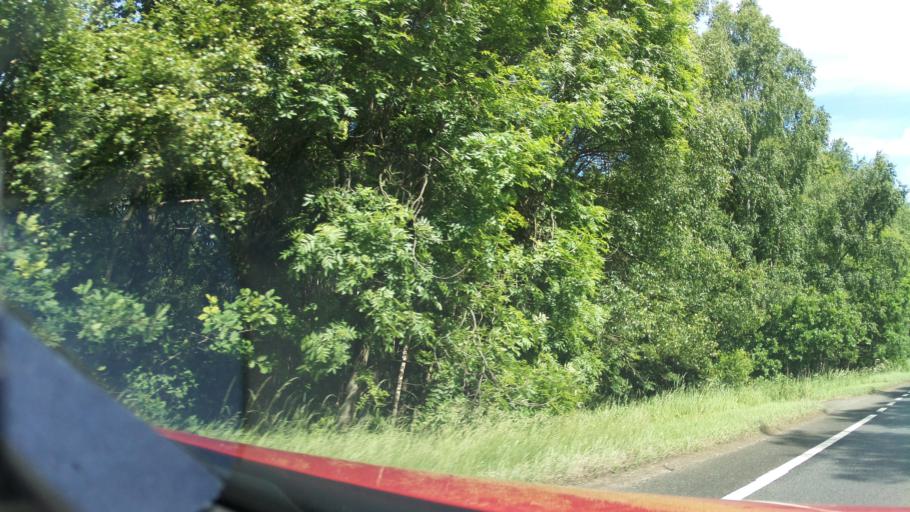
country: GB
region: England
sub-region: Lincolnshire
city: Skellingthorpe
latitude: 53.2171
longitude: -0.6176
